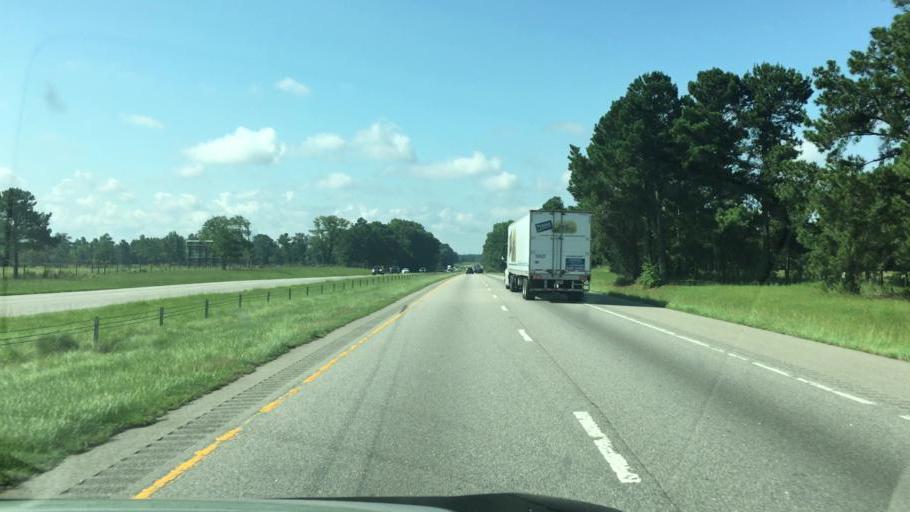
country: US
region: North Carolina
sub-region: Robeson County
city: Saint Pauls
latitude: 34.8669
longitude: -78.9643
